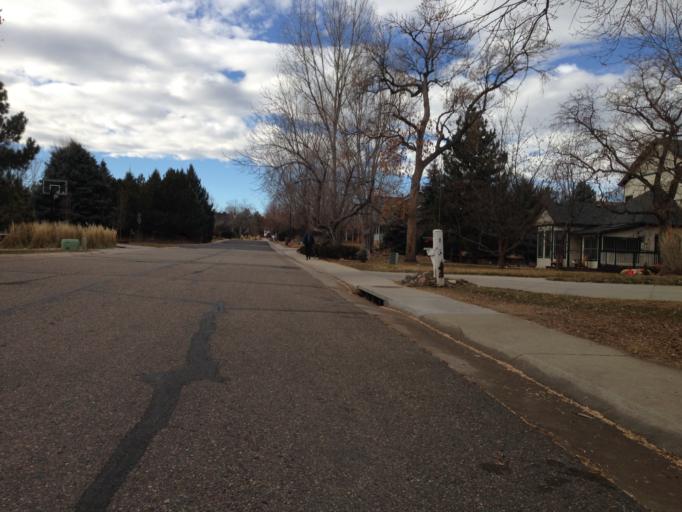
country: US
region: Colorado
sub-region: Boulder County
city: Louisville
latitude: 39.9777
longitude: -105.1434
